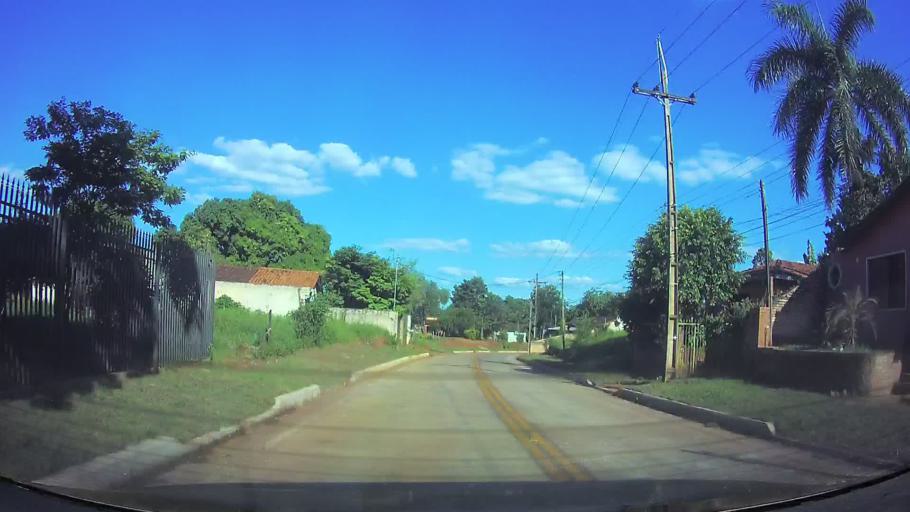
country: PY
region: Cordillera
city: Caacupe
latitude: -25.3720
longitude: -57.1393
